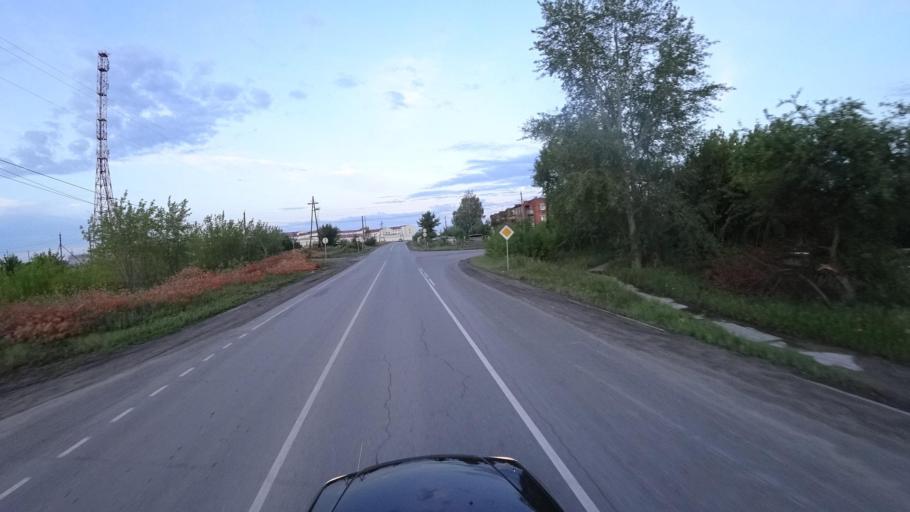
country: RU
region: Sverdlovsk
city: Kamyshlov
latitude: 56.8570
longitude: 62.7306
